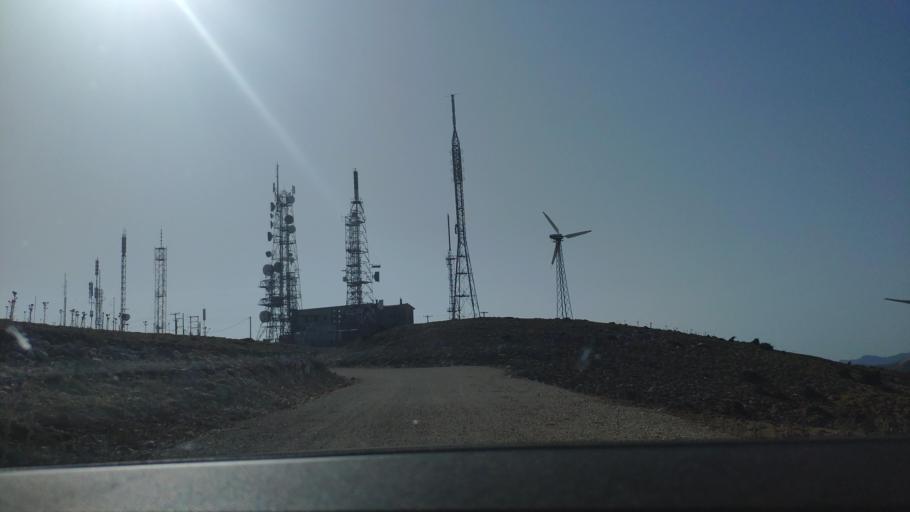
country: GR
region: West Greece
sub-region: Nomos Aitolias kai Akarnanias
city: Monastirakion
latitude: 38.8083
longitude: 20.9831
